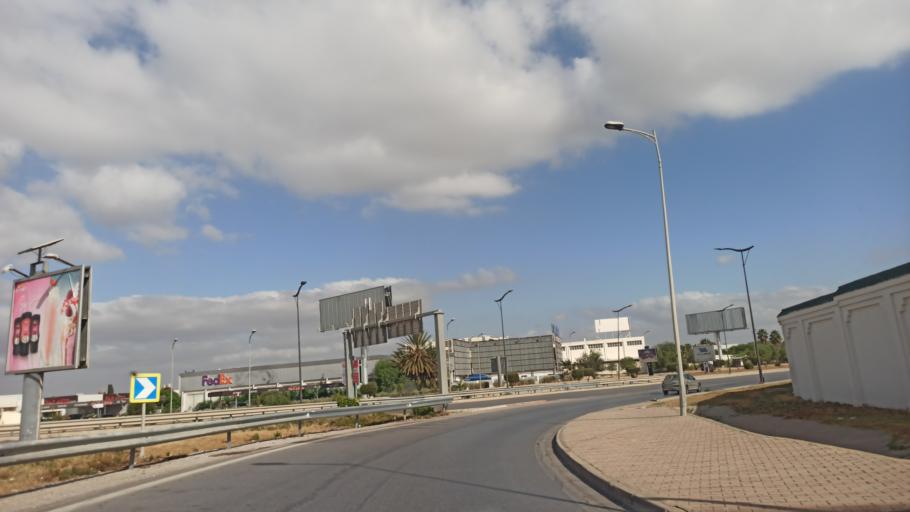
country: TN
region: Ariana
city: Ariana
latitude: 36.8327
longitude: 10.2126
